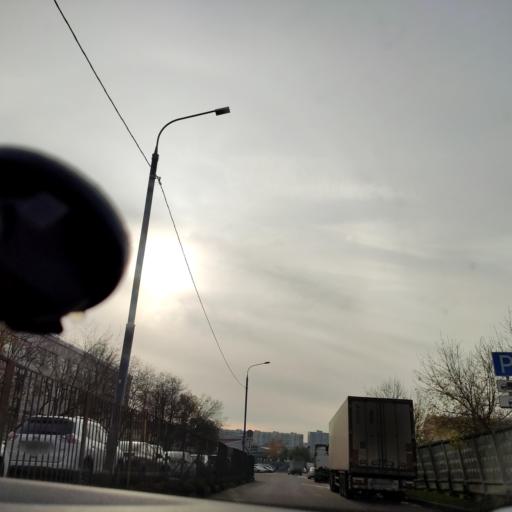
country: RU
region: Moskovskaya
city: Vostochnoe Degunino
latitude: 55.8859
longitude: 37.5528
